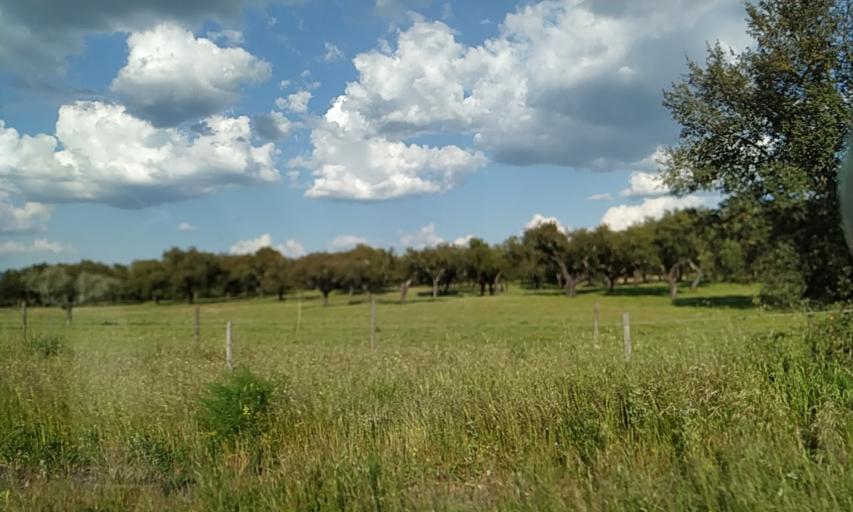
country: PT
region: Portalegre
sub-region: Portalegre
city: Urra
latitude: 39.2268
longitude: -7.4555
